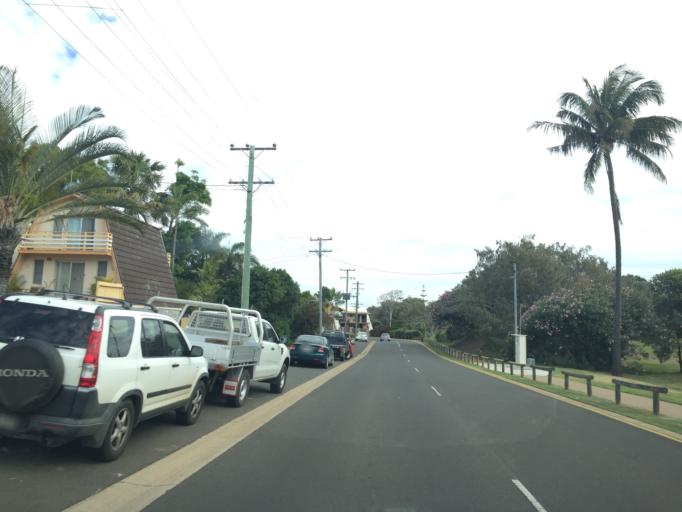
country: AU
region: Queensland
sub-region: Bundaberg
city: Bundaberg
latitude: -24.8200
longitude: 152.4651
